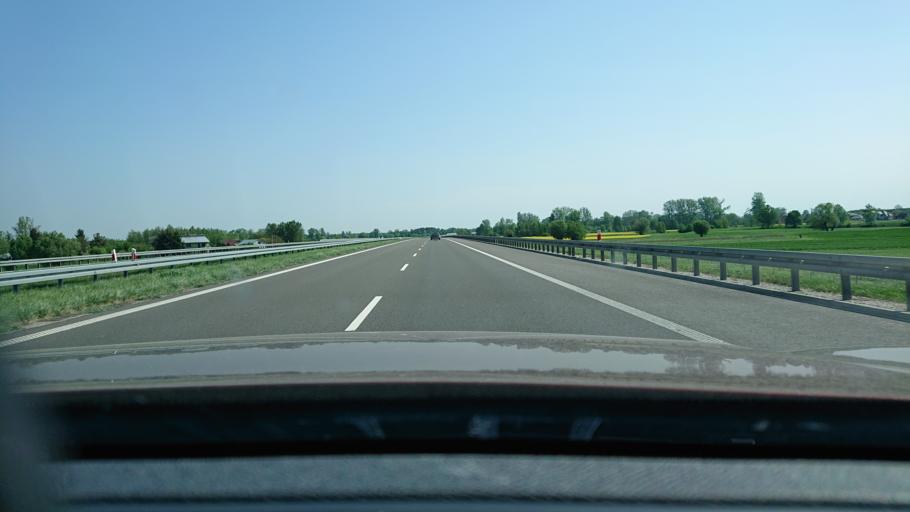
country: PL
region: Subcarpathian Voivodeship
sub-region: Powiat lancucki
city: Bialobrzegi
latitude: 50.1093
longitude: 22.2987
